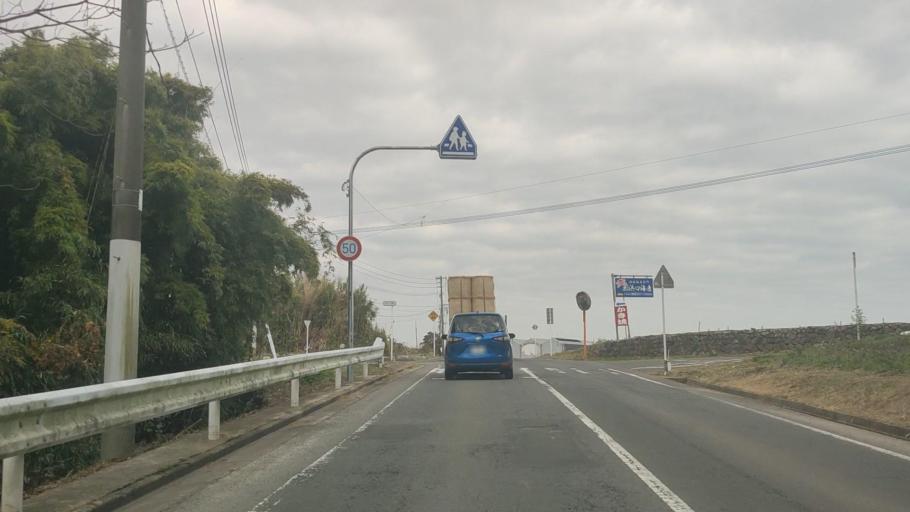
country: JP
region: Nagasaki
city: Shimabara
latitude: 32.8390
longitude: 130.2142
